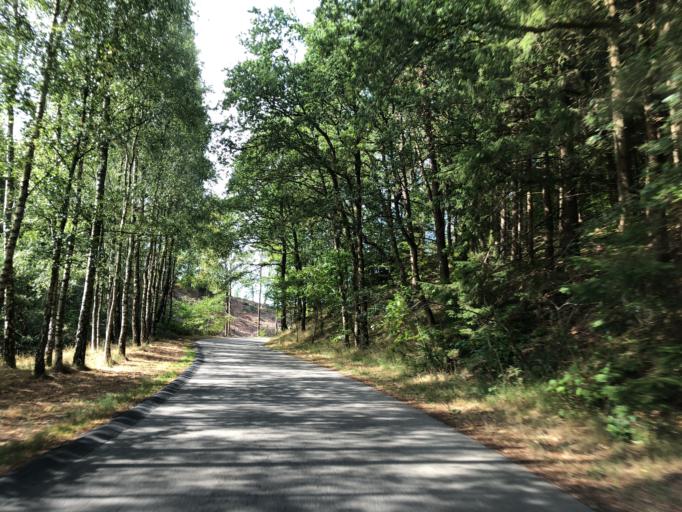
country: DK
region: South Denmark
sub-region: Vejle Kommune
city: Egtved
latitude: 55.6629
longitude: 9.3038
